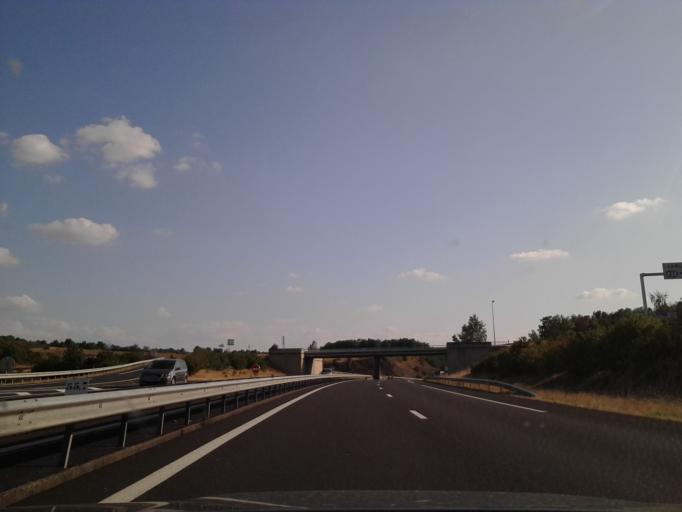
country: FR
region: Auvergne
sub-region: Departement de la Haute-Loire
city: Bournoncle-Saint-Pierre
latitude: 45.3371
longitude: 3.2752
